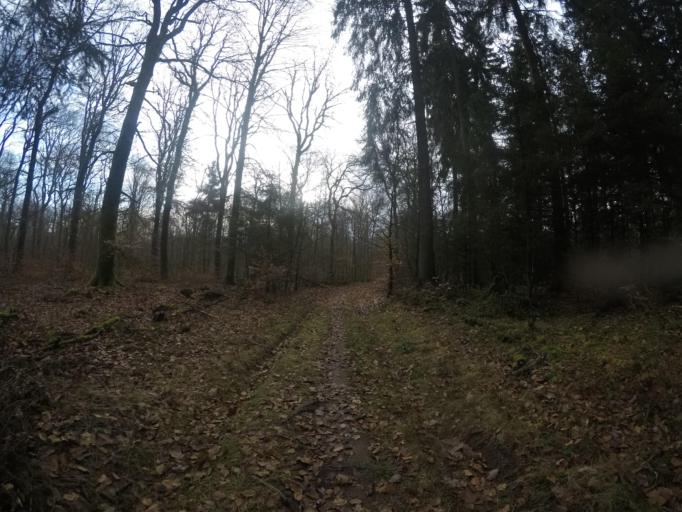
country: BE
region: Wallonia
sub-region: Province du Luxembourg
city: Habay-la-Vieille
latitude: 49.7568
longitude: 5.6009
